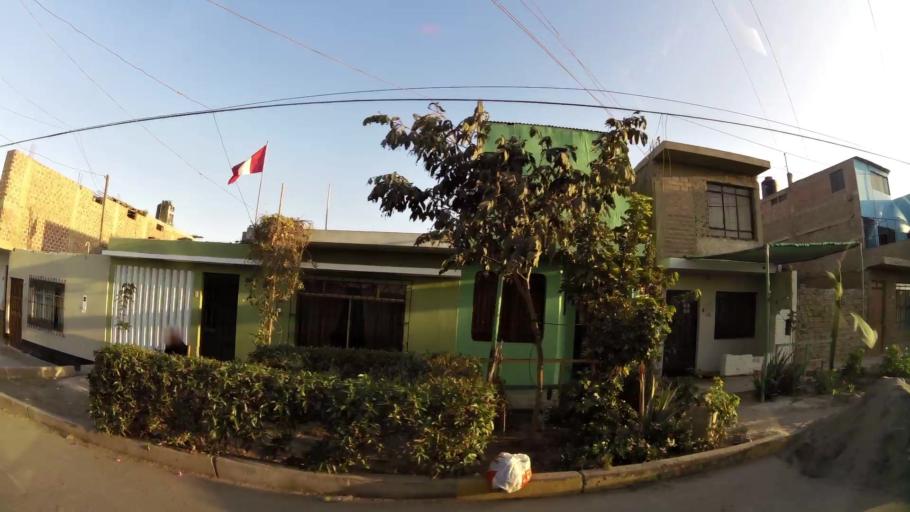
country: PE
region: Ica
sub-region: Provincia de Pisco
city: Villa Tupac Amaru
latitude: -13.7040
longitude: -76.1529
